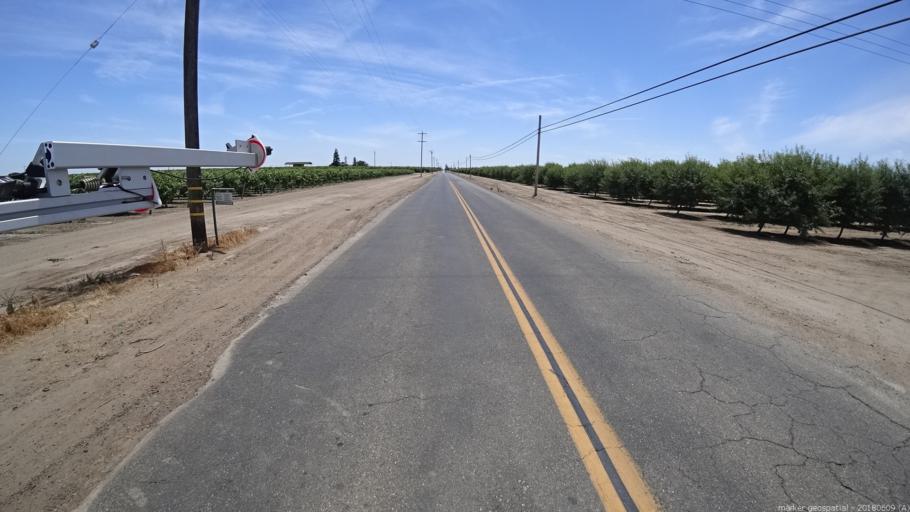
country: US
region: California
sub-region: Madera County
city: Parkwood
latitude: 36.8947
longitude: -120.0923
